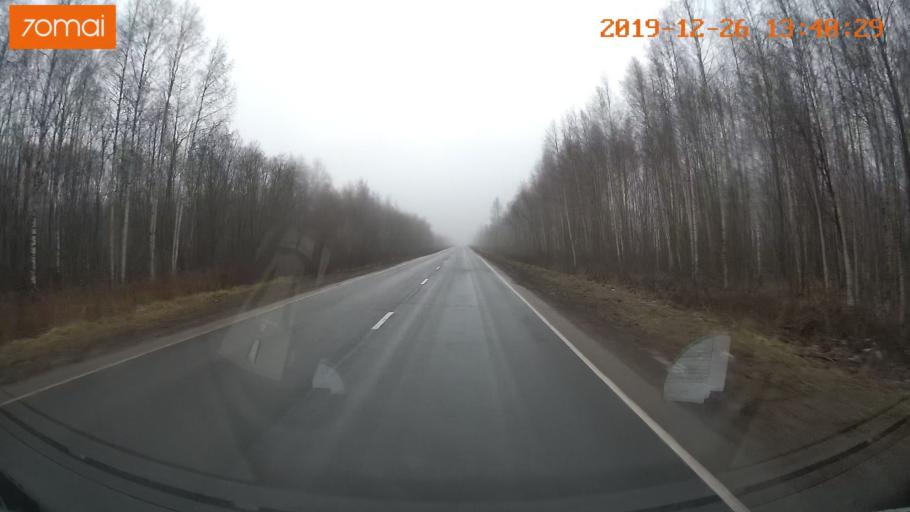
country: RU
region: Vologda
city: Sheksna
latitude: 58.7419
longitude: 38.4307
